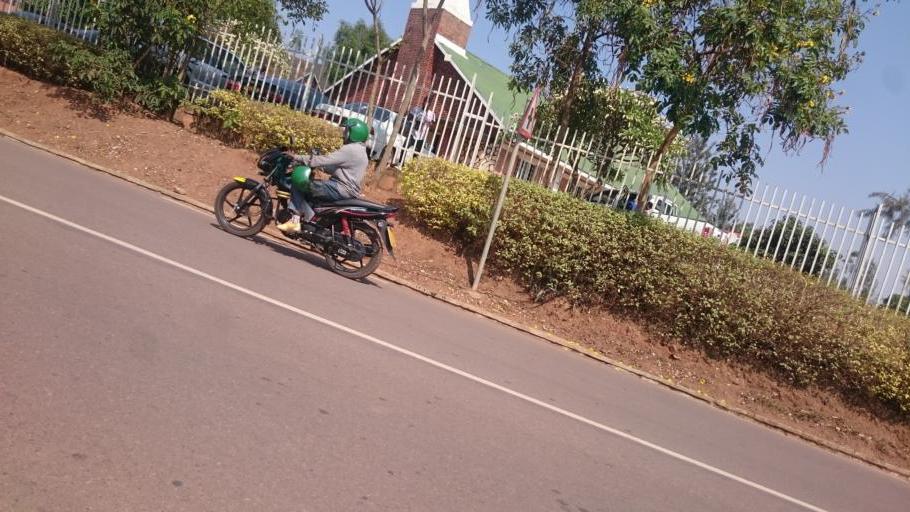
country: RW
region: Kigali
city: Kigali
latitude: -1.9424
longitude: 30.0890
